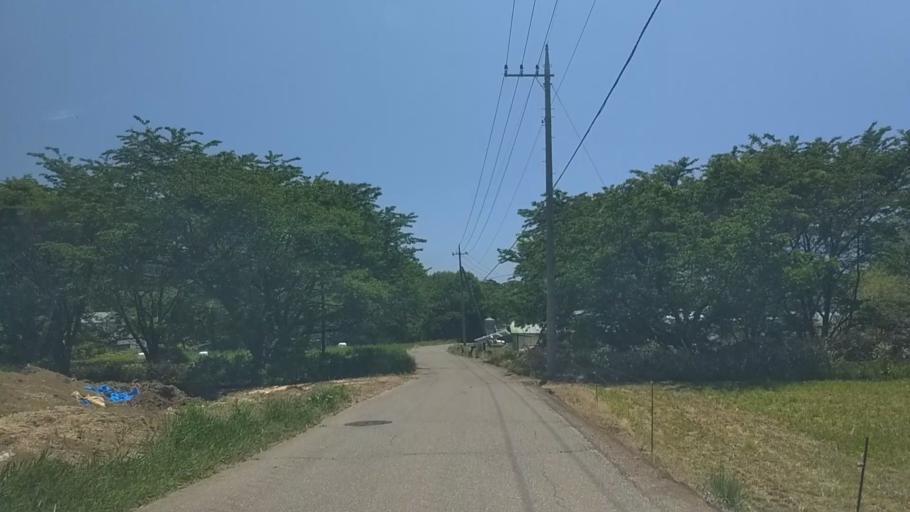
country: JP
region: Yamanashi
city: Nirasaki
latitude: 35.8852
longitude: 138.4362
